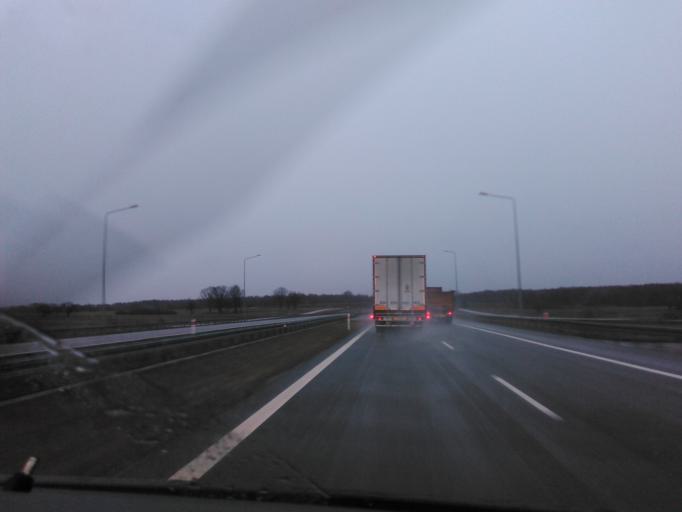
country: PL
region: Masovian Voivodeship
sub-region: Powiat minski
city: Jakubow
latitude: 52.2032
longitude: 21.7293
